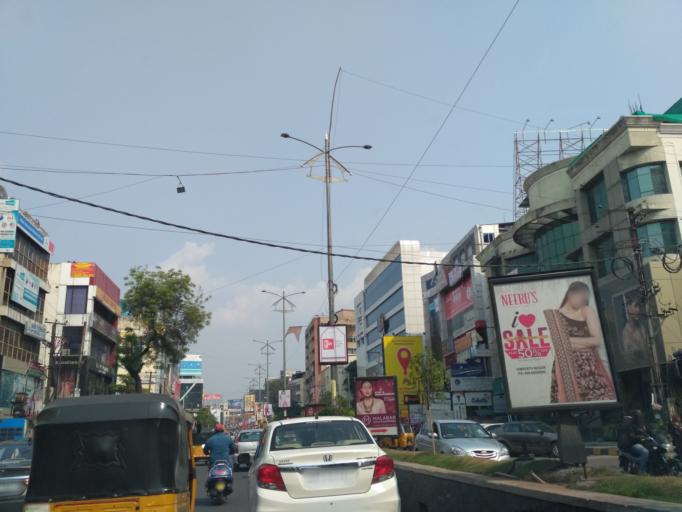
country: IN
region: Telangana
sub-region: Hyderabad
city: Hyderabad
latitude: 17.4019
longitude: 78.4845
